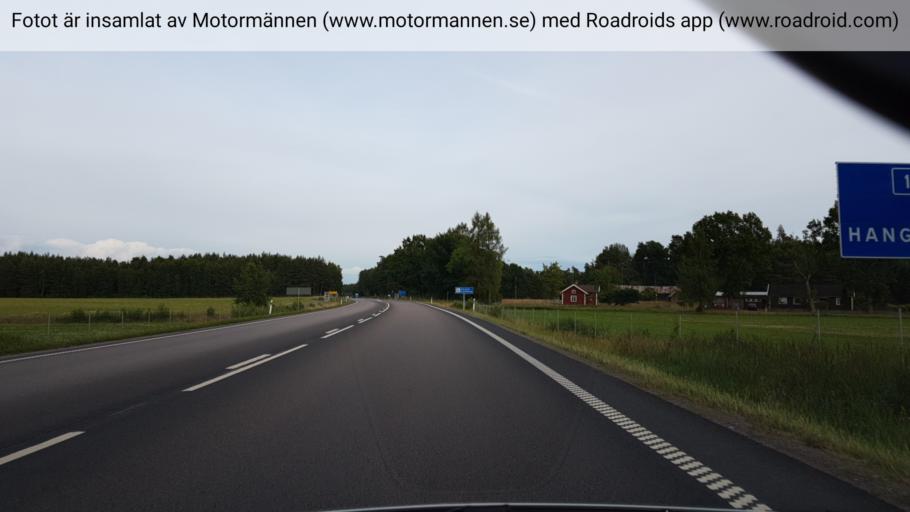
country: SE
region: Vaestra Goetaland
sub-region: Lidkopings Kommun
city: Vinninga
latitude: 58.4218
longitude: 13.3431
